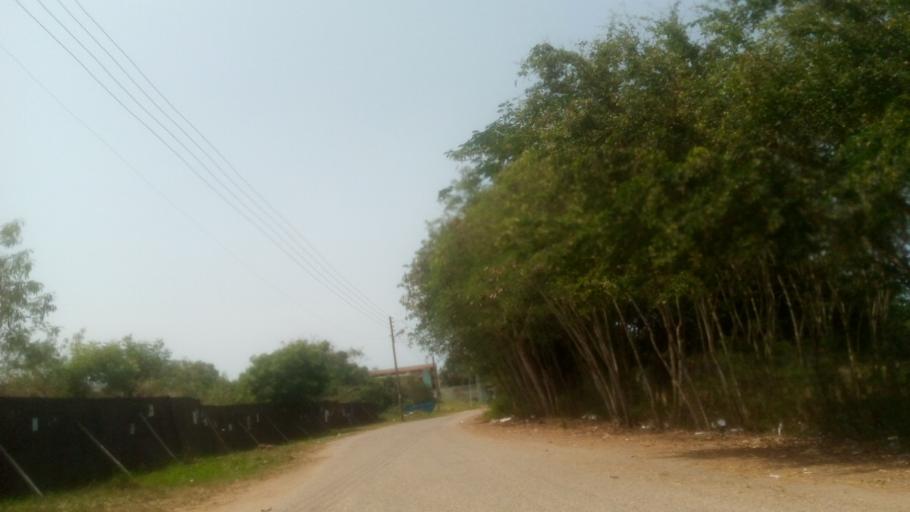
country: GH
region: Central
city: Winneba
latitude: 5.3657
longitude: -0.6333
